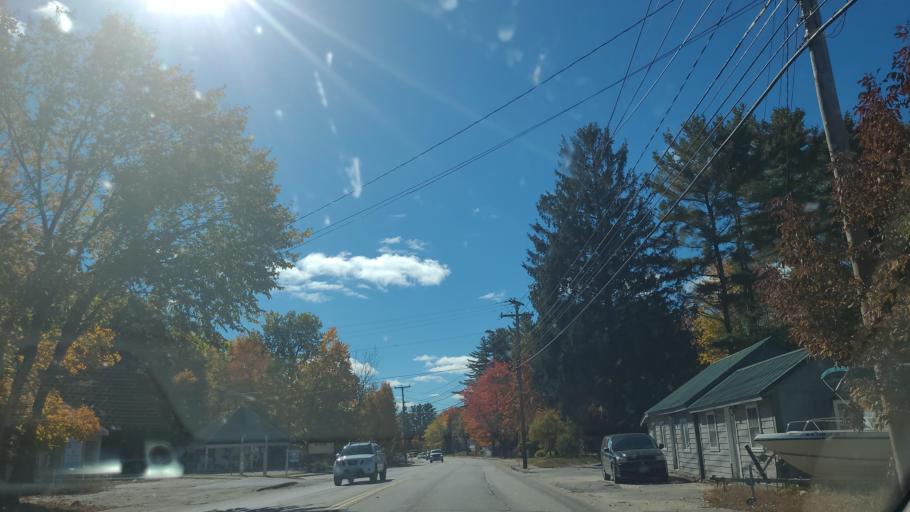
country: US
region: Maine
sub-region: Cumberland County
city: Bridgton
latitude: 44.0508
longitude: -70.7013
